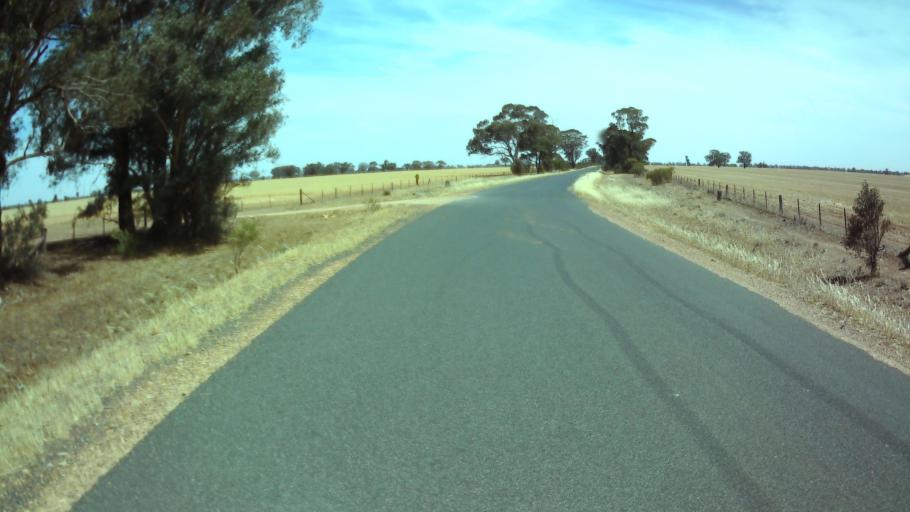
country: AU
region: New South Wales
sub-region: Weddin
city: Grenfell
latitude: -33.9613
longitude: 147.7818
